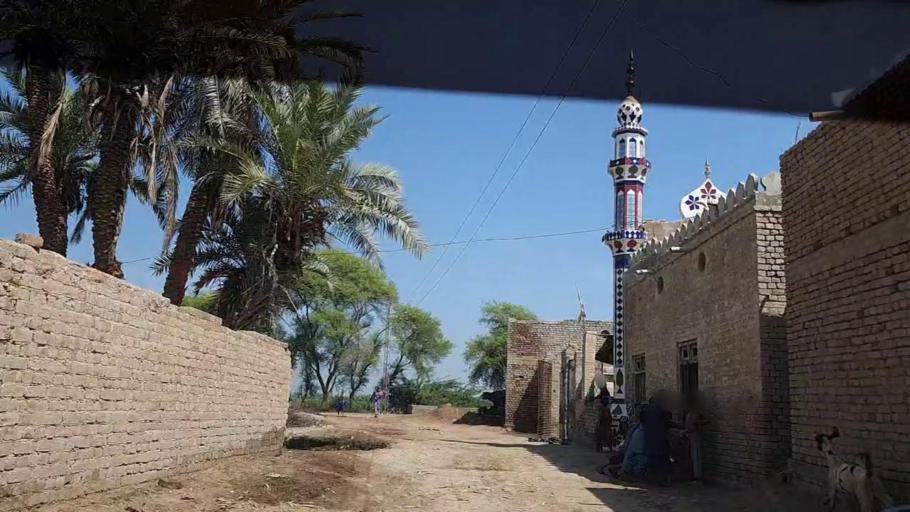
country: PK
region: Sindh
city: Tangwani
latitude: 28.2855
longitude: 69.0389
